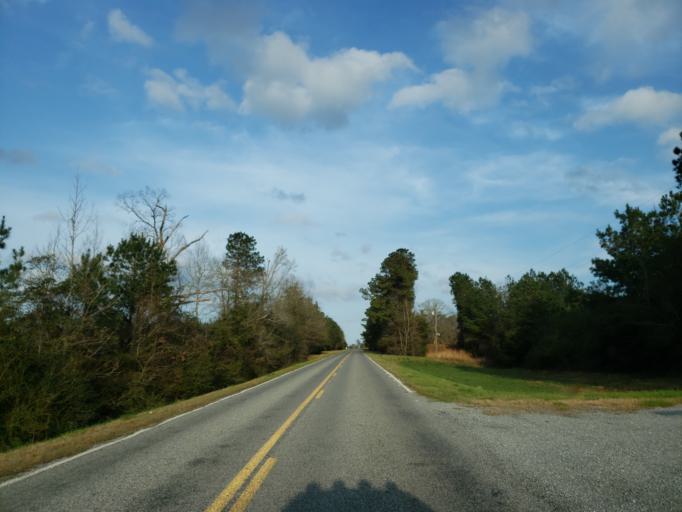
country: US
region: Mississippi
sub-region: Clarke County
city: Stonewall
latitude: 32.1721
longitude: -88.6916
